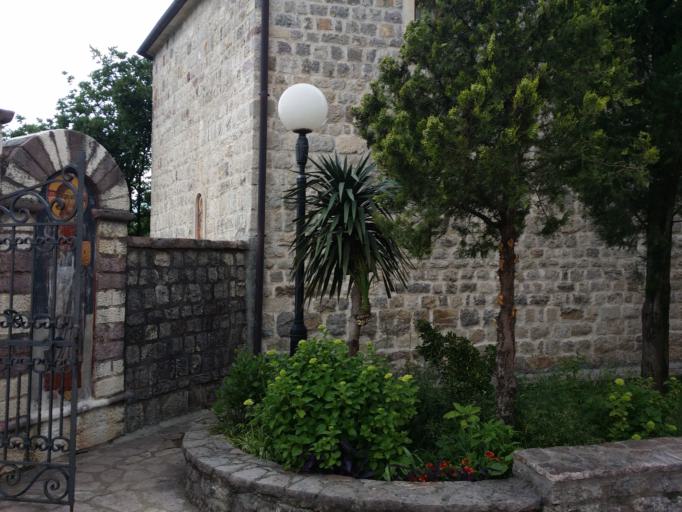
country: ME
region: Budva
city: Budva
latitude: 42.2979
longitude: 18.8447
